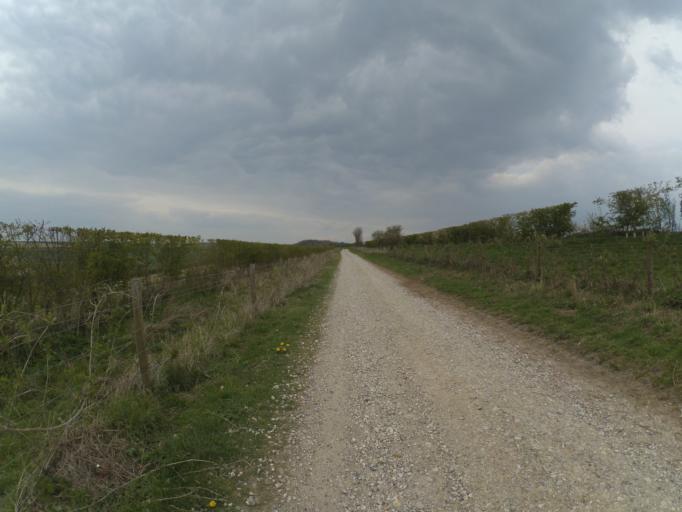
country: GB
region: England
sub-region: West Sussex
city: Arundel
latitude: 50.8824
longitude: -0.5216
